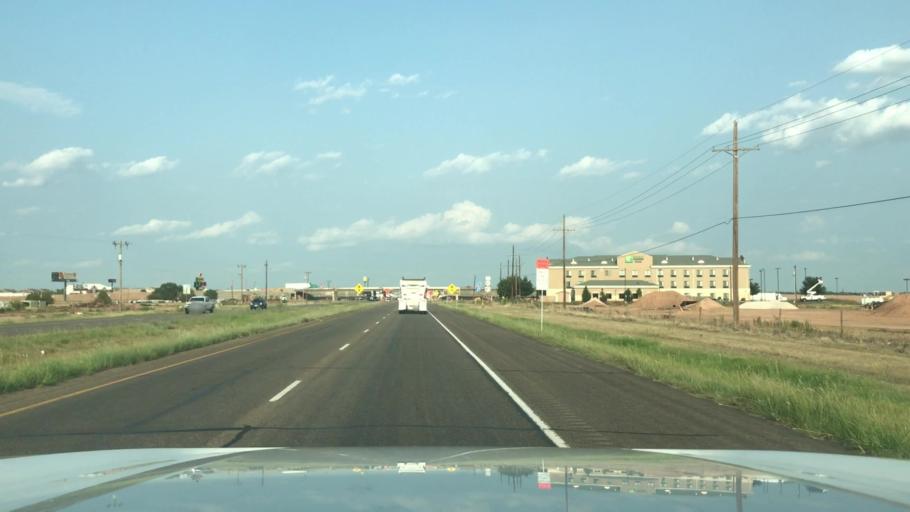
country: US
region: Texas
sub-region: Potter County
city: Amarillo
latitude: 35.1167
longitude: -101.9152
